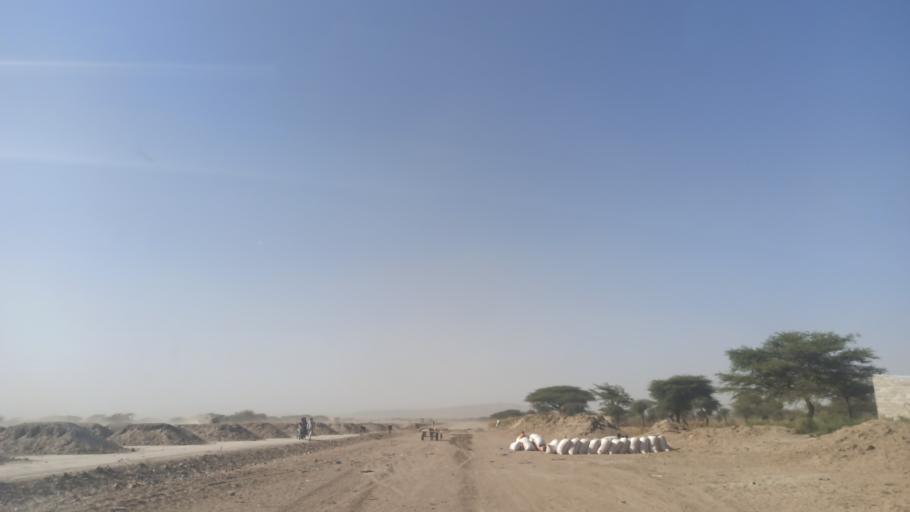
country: ET
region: Oromiya
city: Ziway
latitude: 7.7397
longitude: 38.6208
